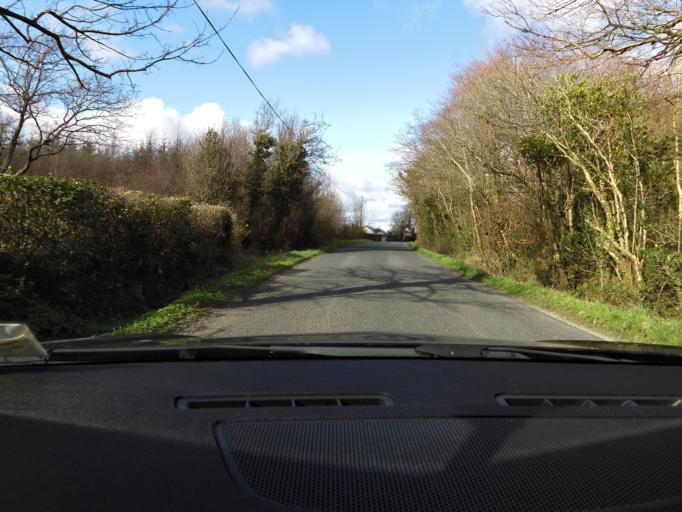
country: IE
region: Connaught
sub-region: County Galway
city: Athenry
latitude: 53.4601
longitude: -8.5496
